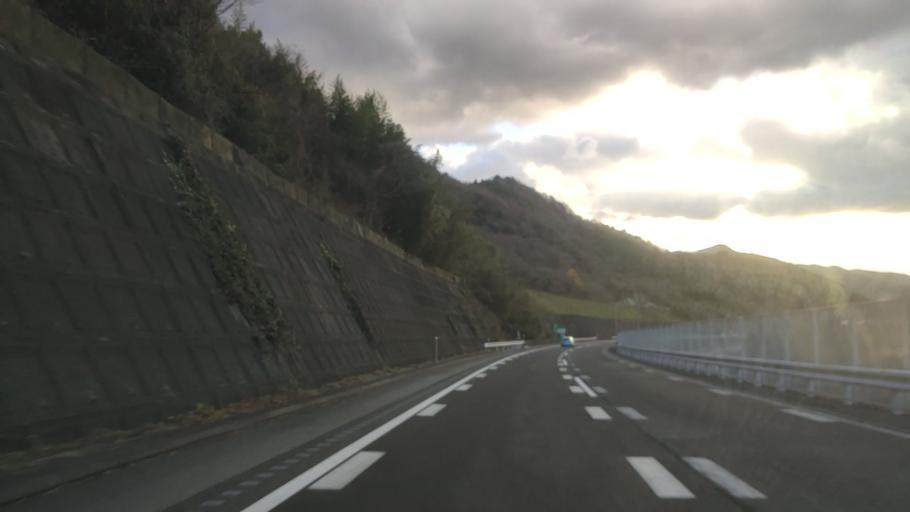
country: JP
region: Ehime
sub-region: Shikoku-chuo Shi
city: Matsuyama
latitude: 33.8057
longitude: 132.9439
